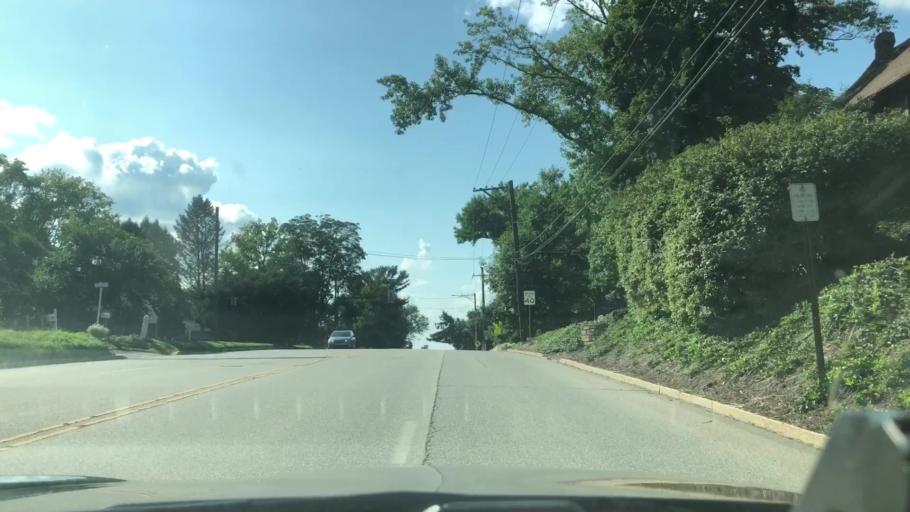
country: US
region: Pennsylvania
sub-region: Montgomery County
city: Wyndmoor
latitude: 40.0941
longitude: -75.1916
